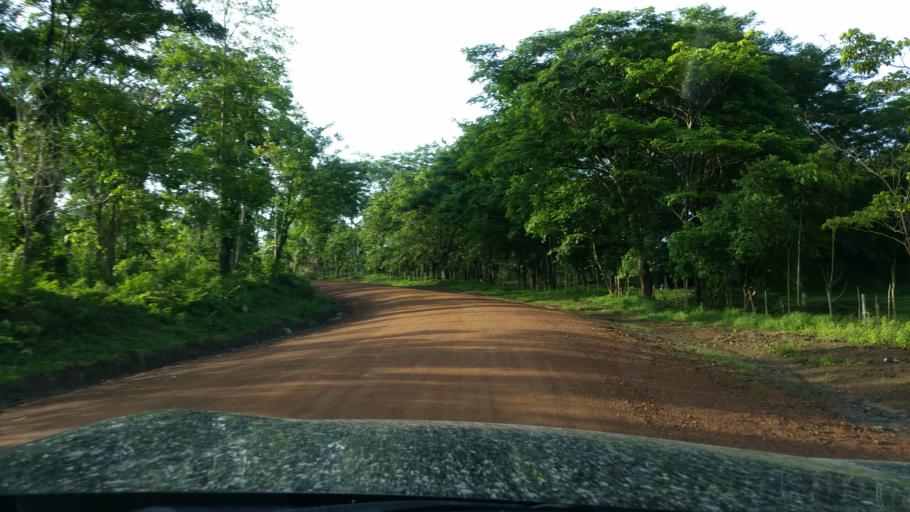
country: NI
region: Atlantico Norte (RAAN)
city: Puerto Cabezas
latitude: 14.0682
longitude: -83.9739
